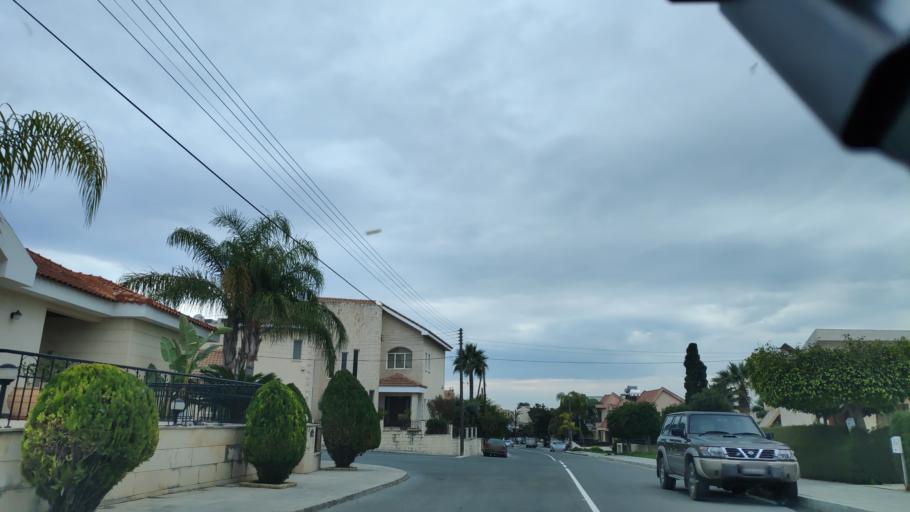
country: CY
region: Limassol
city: Limassol
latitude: 34.7001
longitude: 33.0266
